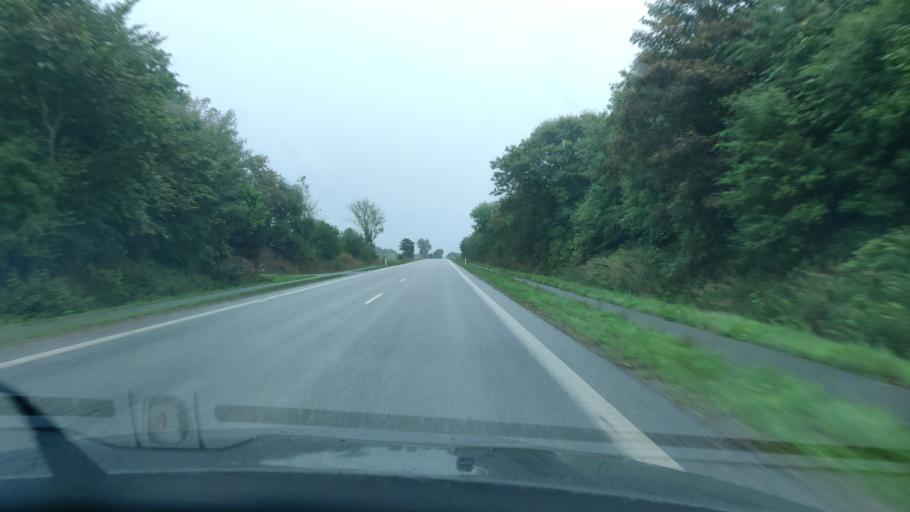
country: DK
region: North Denmark
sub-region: Morso Kommune
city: Nykobing Mors
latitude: 57.0315
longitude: 8.9850
